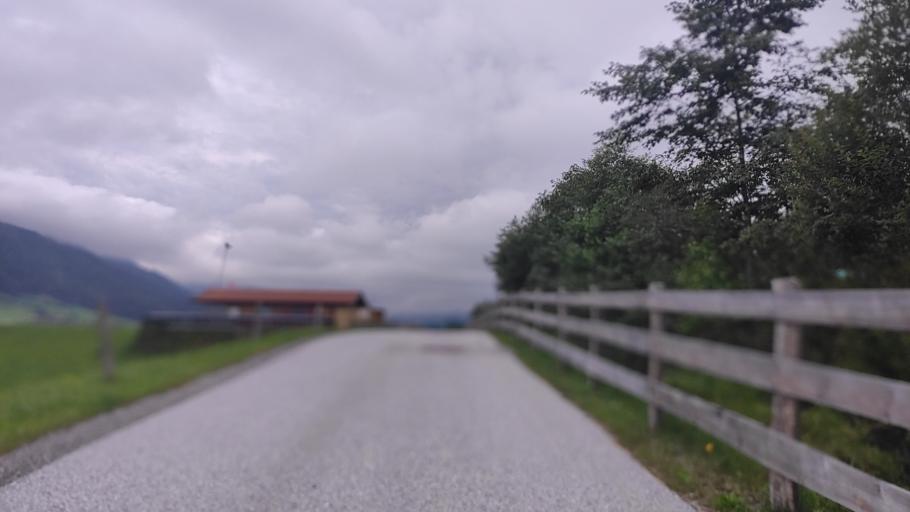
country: AT
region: Salzburg
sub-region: Politischer Bezirk Zell am See
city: Mittersill
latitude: 47.2838
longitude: 12.4656
